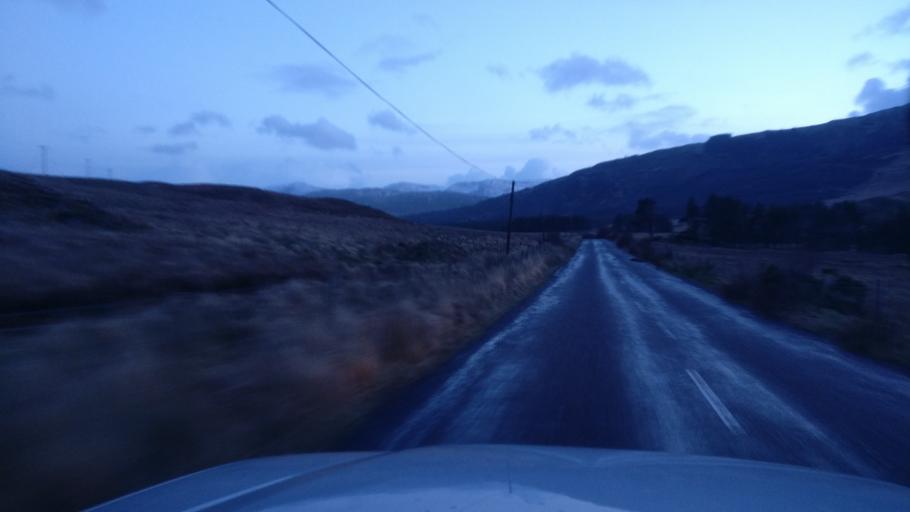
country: IE
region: Connaught
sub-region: Maigh Eo
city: Westport
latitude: 53.5615
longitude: -9.6486
